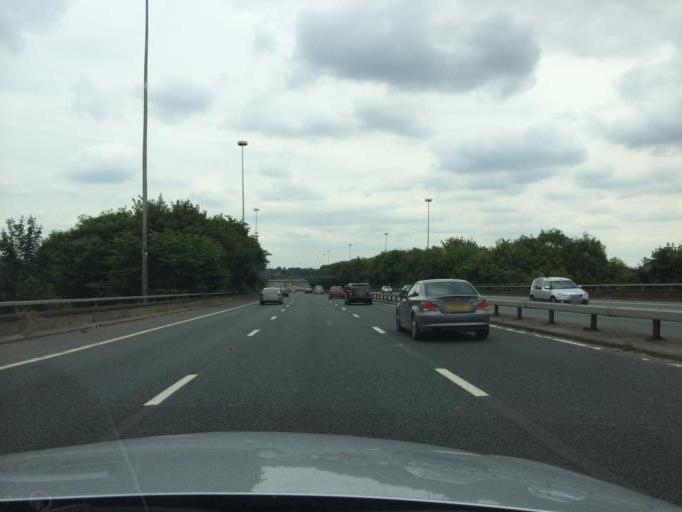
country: GB
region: England
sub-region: Knowsley
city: Huyton
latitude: 53.4063
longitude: -2.8916
